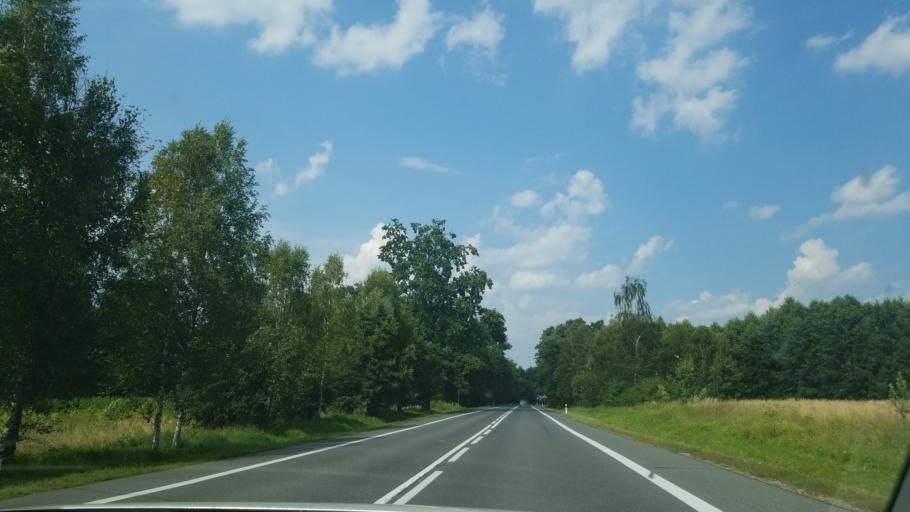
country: PL
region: Subcarpathian Voivodeship
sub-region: Powiat nizanski
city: Zarzecze
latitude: 50.5461
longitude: 22.2285
